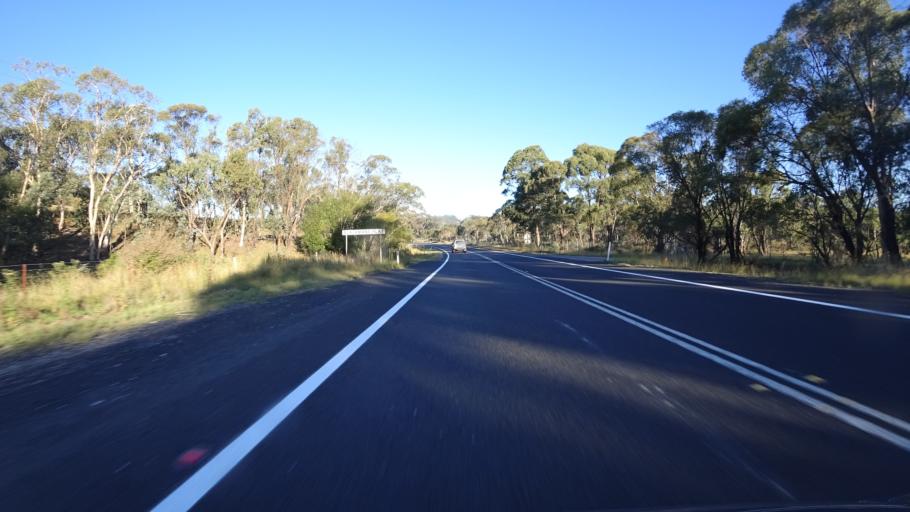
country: AU
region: New South Wales
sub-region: Lithgow
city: Portland
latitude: -33.3495
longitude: 150.0396
